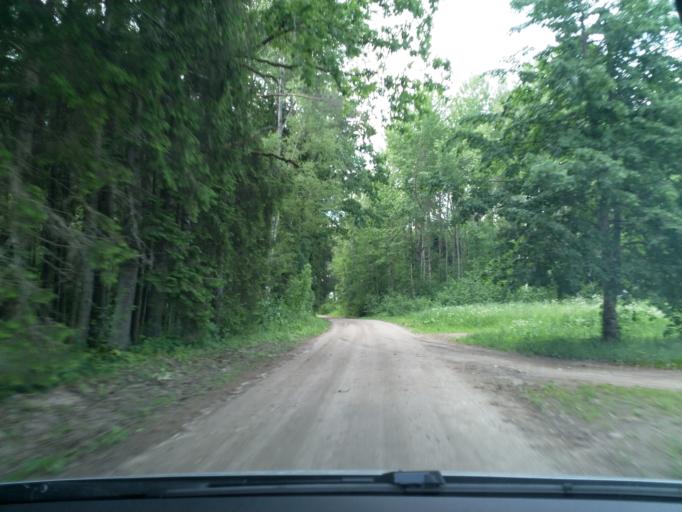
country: LV
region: Kuldigas Rajons
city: Kuldiga
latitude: 56.8373
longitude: 21.9559
